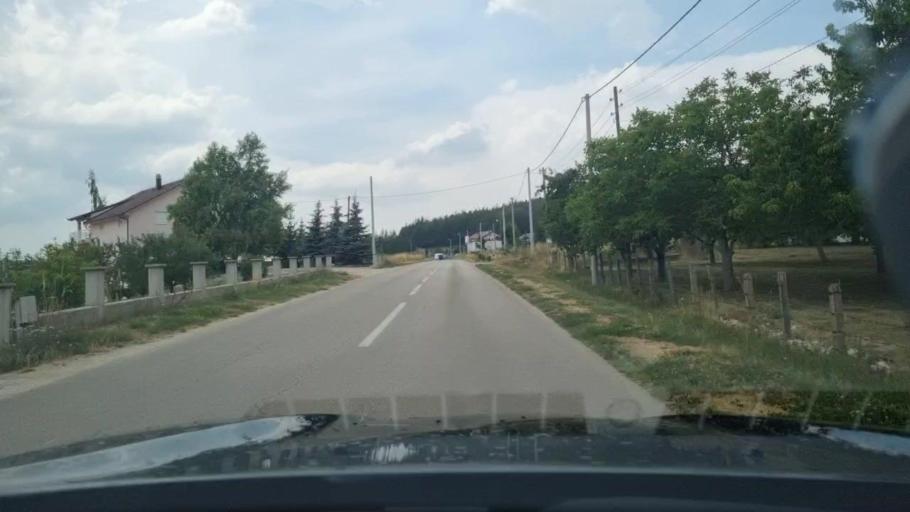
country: BA
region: Federation of Bosnia and Herzegovina
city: Tomislavgrad
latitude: 43.7037
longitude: 17.2139
